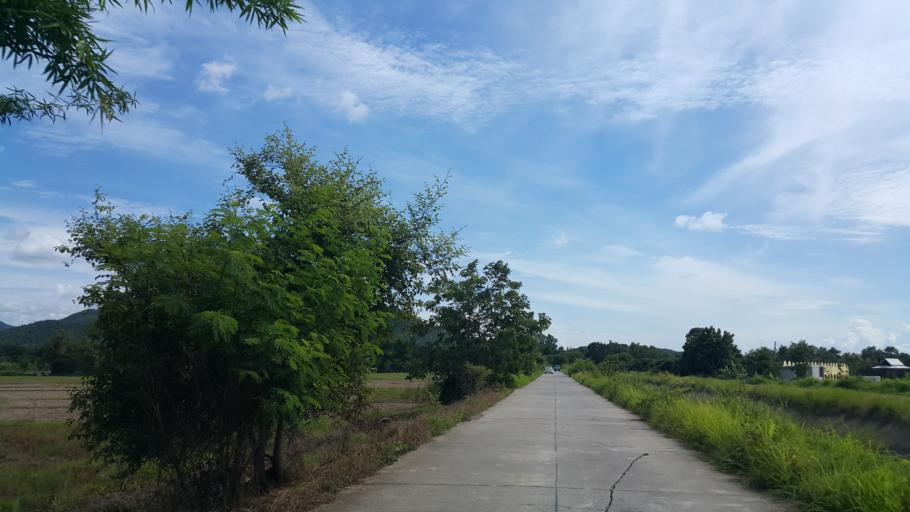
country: TH
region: Chiang Mai
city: Mae On
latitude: 18.7321
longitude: 99.1991
